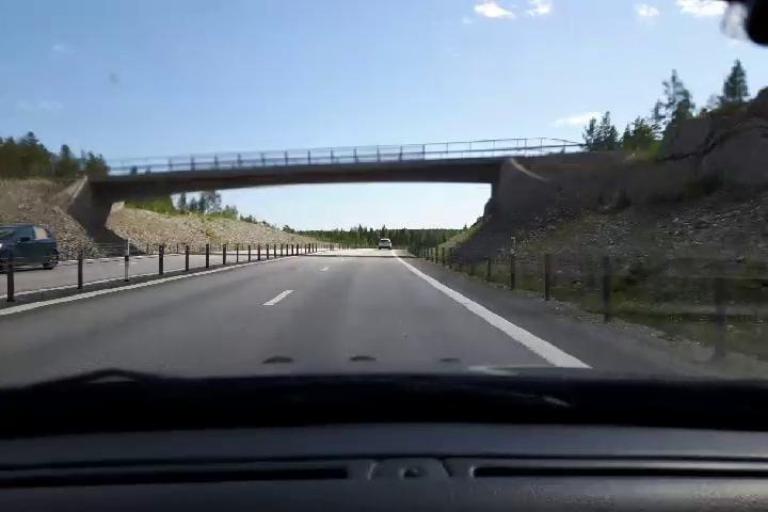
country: SE
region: Gaevleborg
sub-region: Hudiksvalls Kommun
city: Iggesund
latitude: 61.6941
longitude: 17.0572
